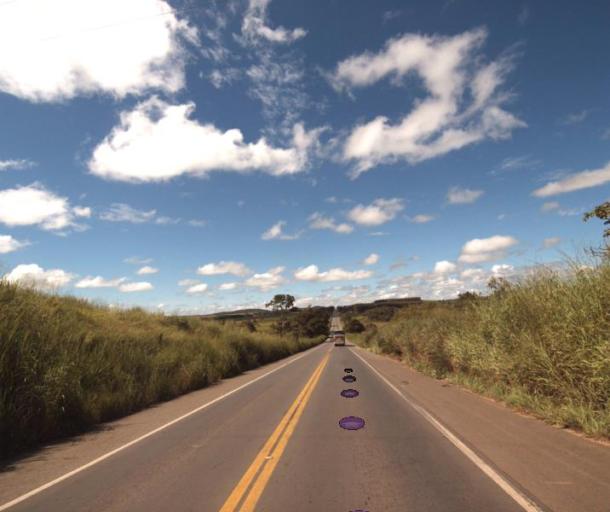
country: BR
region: Goias
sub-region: Rialma
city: Rialma
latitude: -15.4546
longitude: -49.5033
